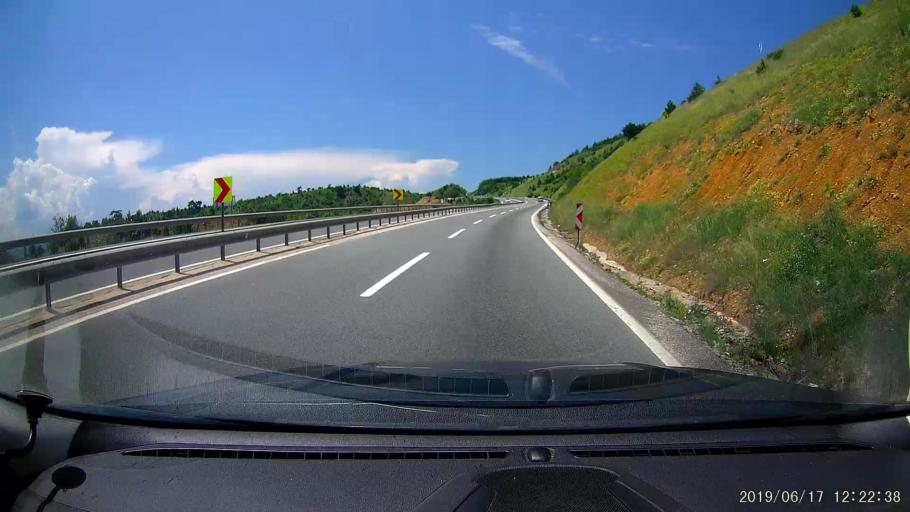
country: TR
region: Karabuk
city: Gozyeri
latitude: 40.8329
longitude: 32.3972
